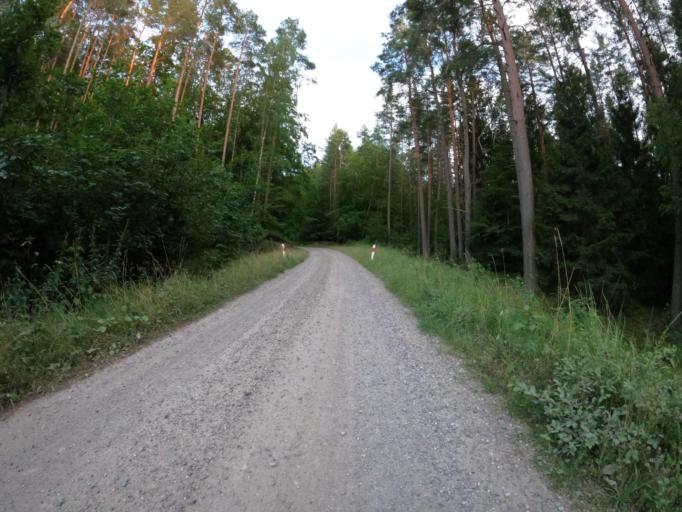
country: PL
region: West Pomeranian Voivodeship
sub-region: Powiat koszalinski
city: Sianow
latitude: 54.1039
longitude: 16.3711
